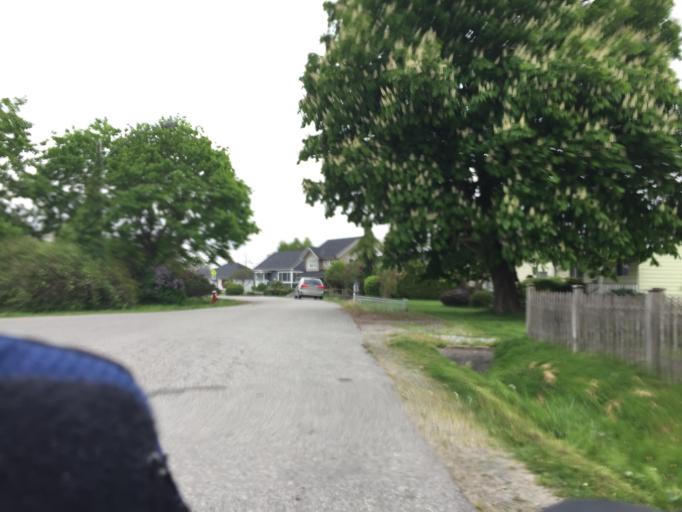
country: CA
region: British Columbia
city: Richmond
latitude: 49.1912
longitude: -123.1473
